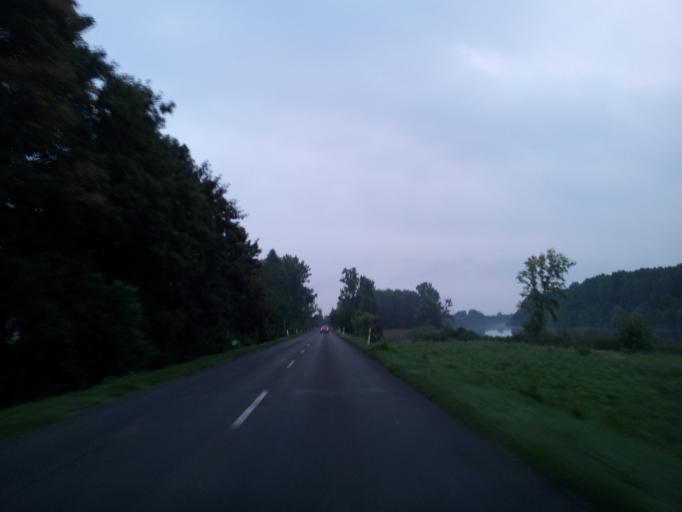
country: HU
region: Tolna
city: Fadd
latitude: 46.4406
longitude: 18.8119
